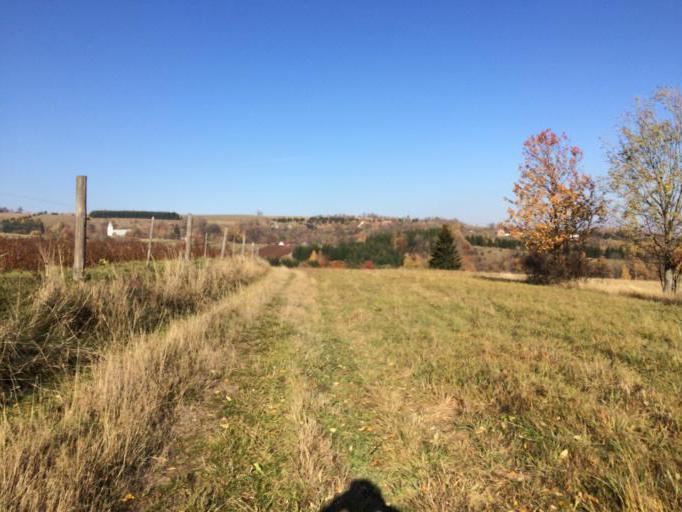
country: PL
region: Lower Silesian Voivodeship
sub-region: Powiat klodzki
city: Miedzylesie
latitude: 50.1948
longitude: 16.6091
